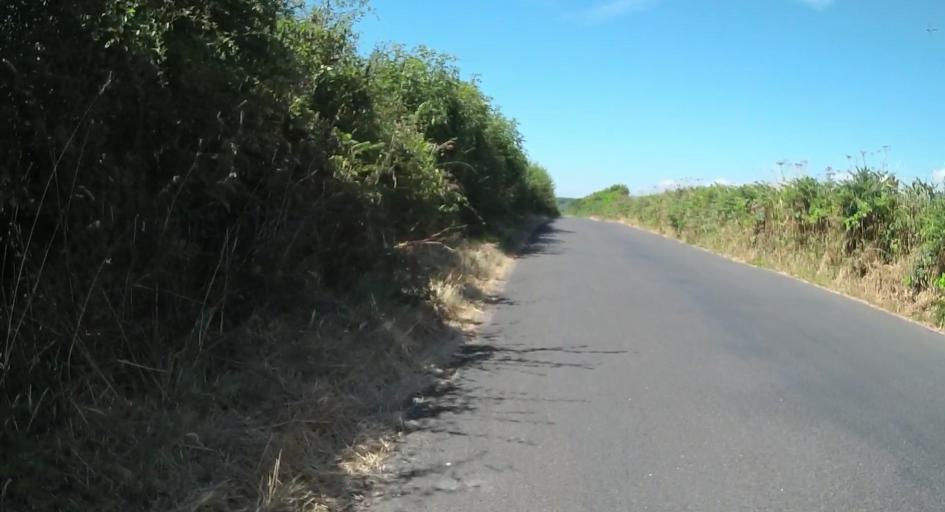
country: GB
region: England
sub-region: Dorset
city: Wool
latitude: 50.6330
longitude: -2.1940
